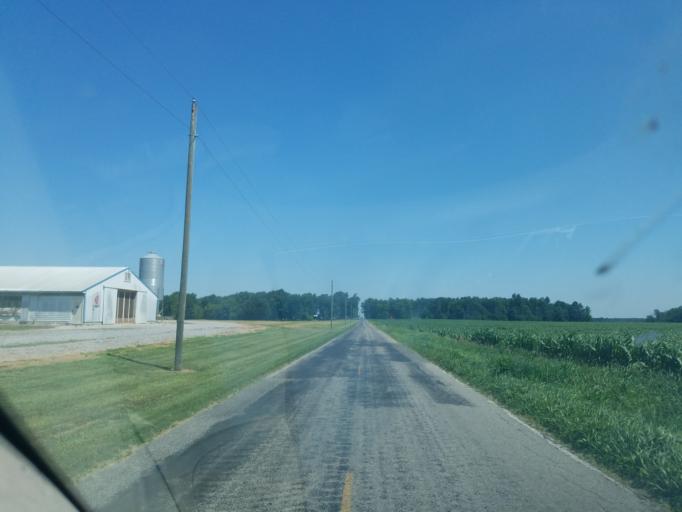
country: US
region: Ohio
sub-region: Mercer County
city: Saint Henry
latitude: 40.4528
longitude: -84.7080
